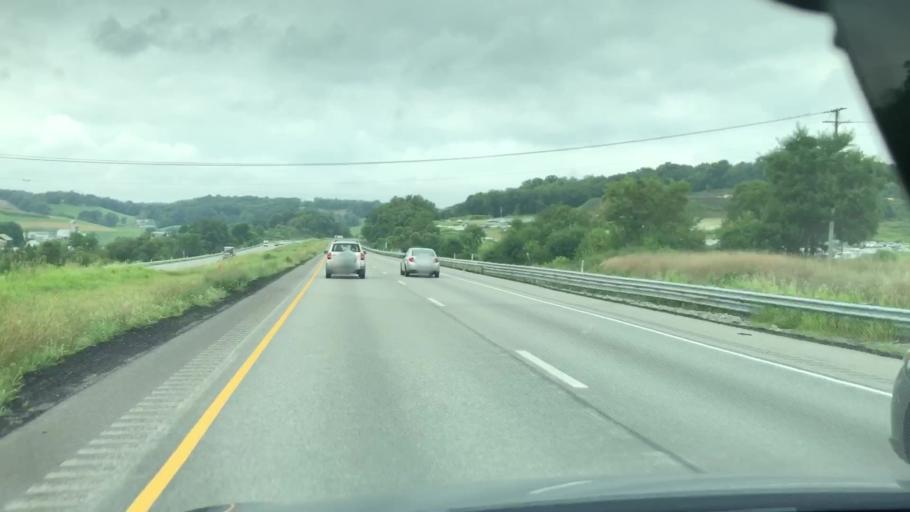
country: US
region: Pennsylvania
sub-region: Butler County
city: Zelienople
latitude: 40.7619
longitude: -80.1208
